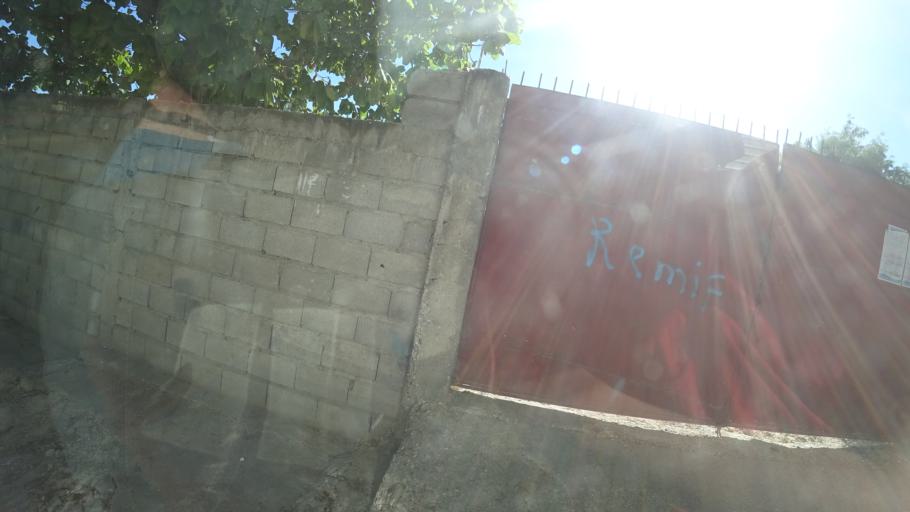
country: HT
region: Ouest
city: Delmas 73
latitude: 18.5464
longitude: -72.3147
